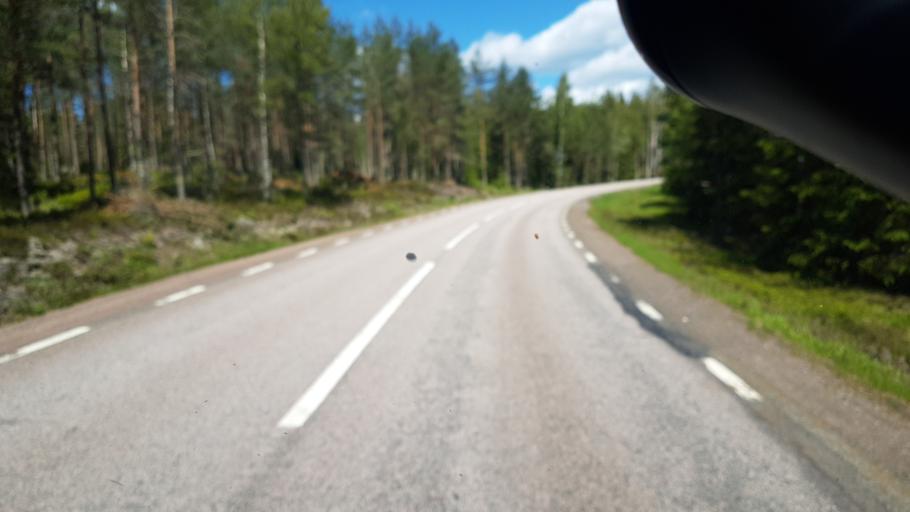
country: SE
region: Vaermland
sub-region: Sunne Kommun
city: Sunne
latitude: 59.6879
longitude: 13.0488
